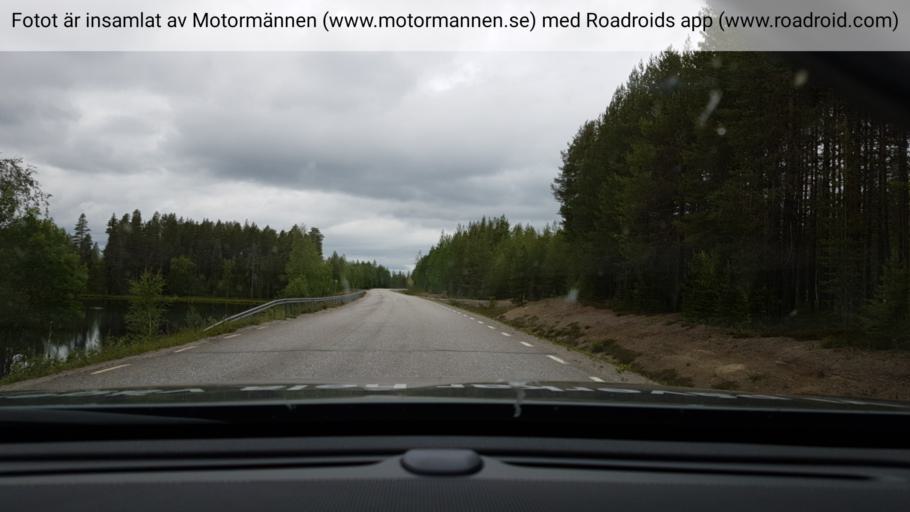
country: SE
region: Vaesterbotten
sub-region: Sorsele Kommun
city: Sorsele
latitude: 65.3102
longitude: 17.6871
